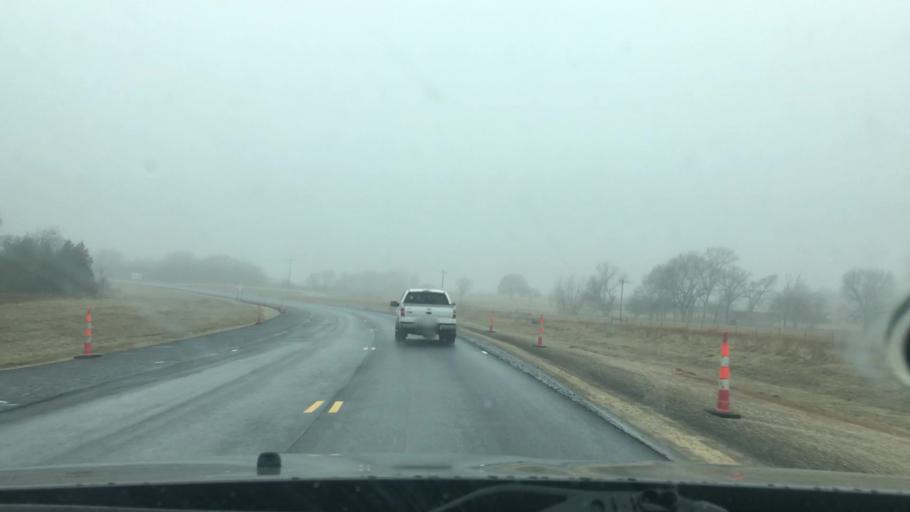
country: US
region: Oklahoma
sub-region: Johnston County
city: Tishomingo
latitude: 34.3205
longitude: -96.6692
